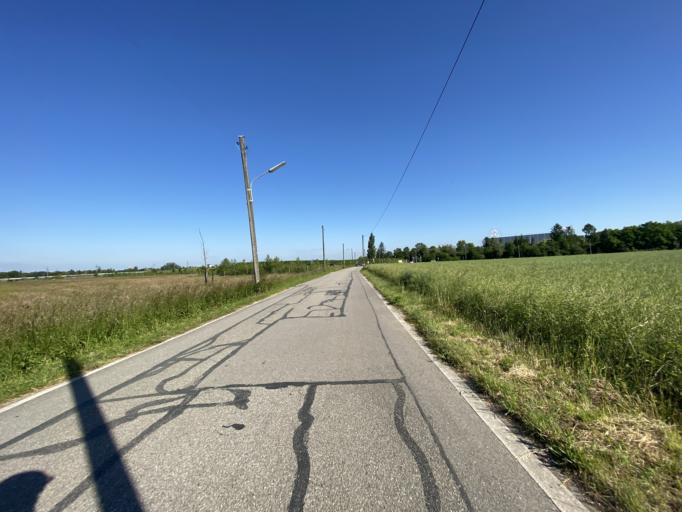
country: DE
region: Bavaria
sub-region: Upper Bavaria
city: Pasing
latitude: 48.1725
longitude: 11.4310
